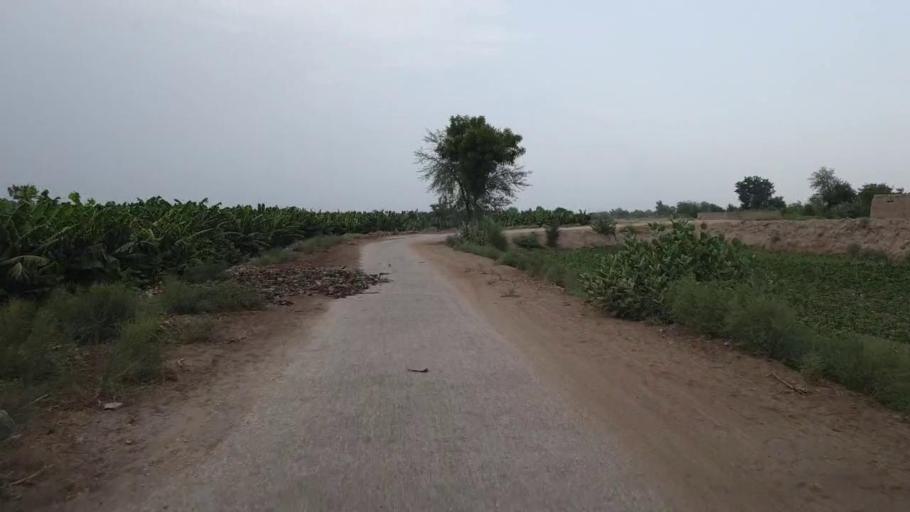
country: PK
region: Sindh
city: Bandhi
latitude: 26.5334
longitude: 68.2015
